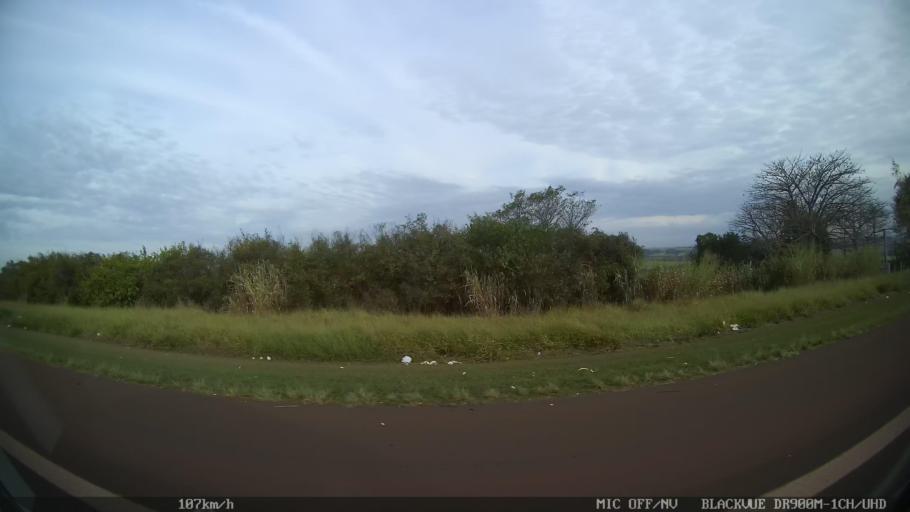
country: BR
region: Sao Paulo
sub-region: Iracemapolis
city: Iracemapolis
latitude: -22.6692
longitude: -47.5413
